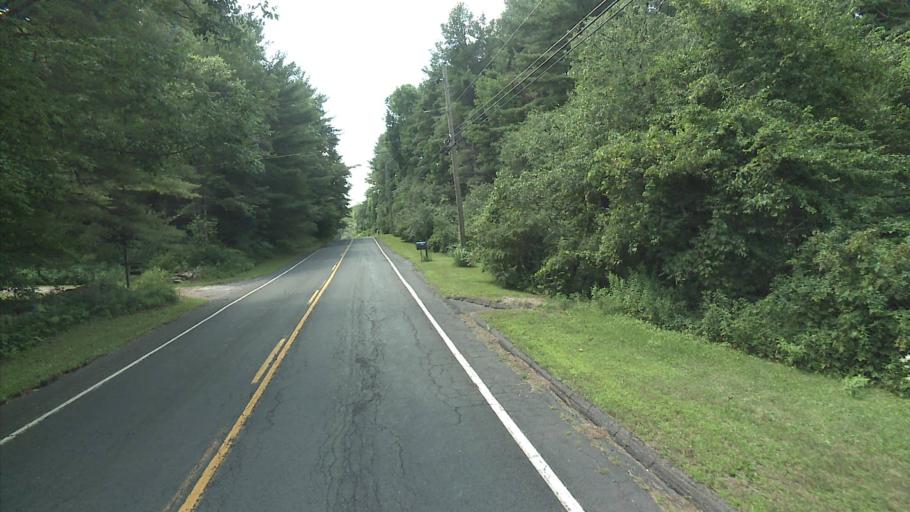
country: US
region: Connecticut
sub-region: Litchfield County
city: Litchfield
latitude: 41.8645
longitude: -73.2975
